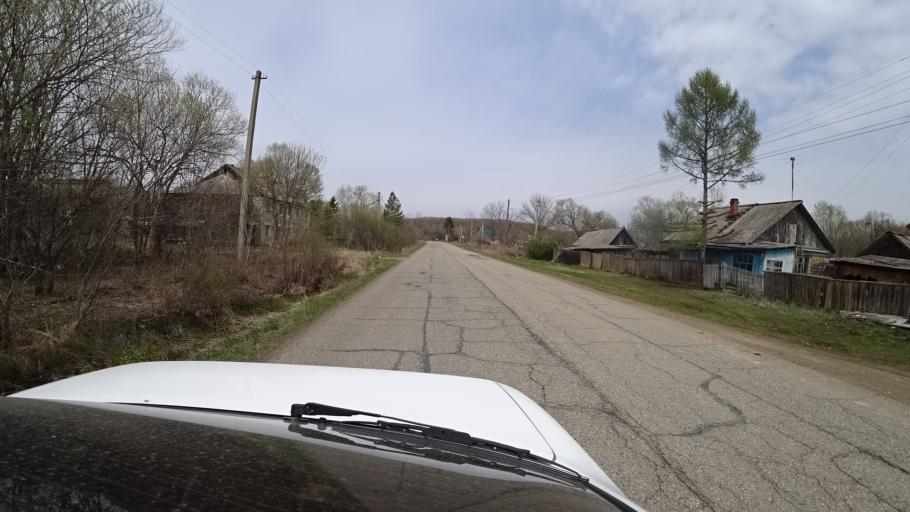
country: RU
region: Primorskiy
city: Novopokrovka
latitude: 45.7870
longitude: 134.1150
